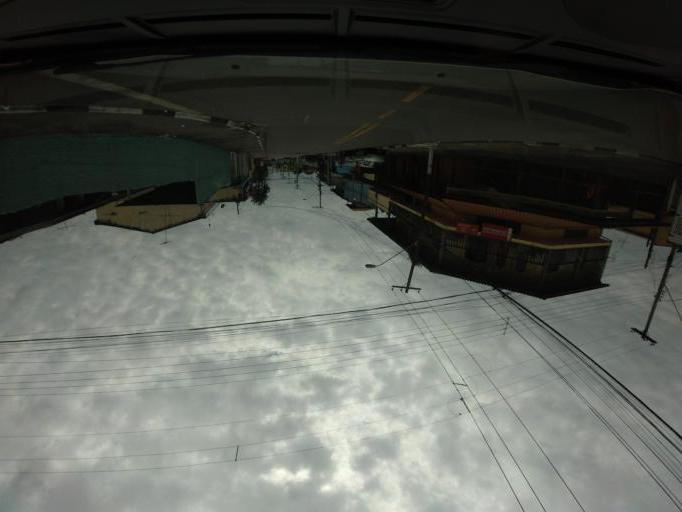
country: BR
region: Sao Paulo
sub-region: Hortolandia
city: Hortolandia
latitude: -22.8414
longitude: -47.1614
